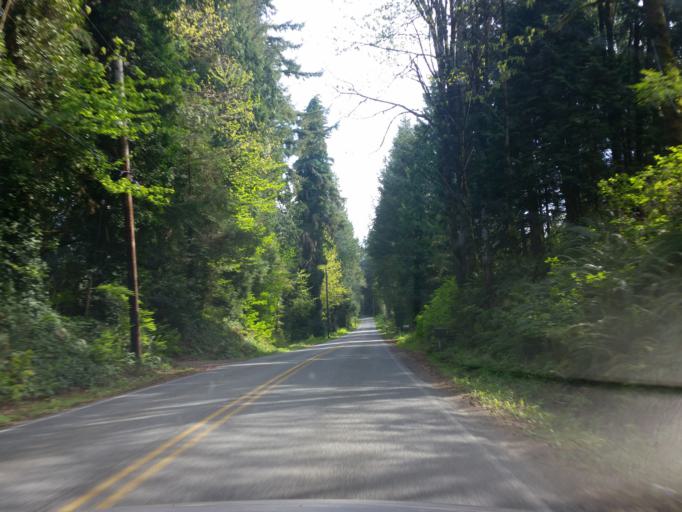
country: US
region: Washington
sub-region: Snohomish County
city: Granite Falls
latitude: 48.0561
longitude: -121.9250
